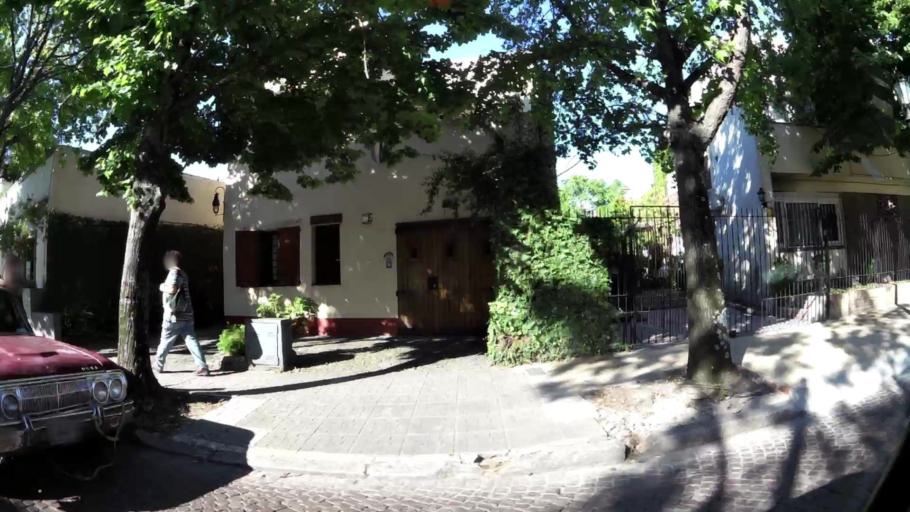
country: AR
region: Buenos Aires
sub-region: Partido de San Isidro
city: San Isidro
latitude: -34.4667
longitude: -58.5126
